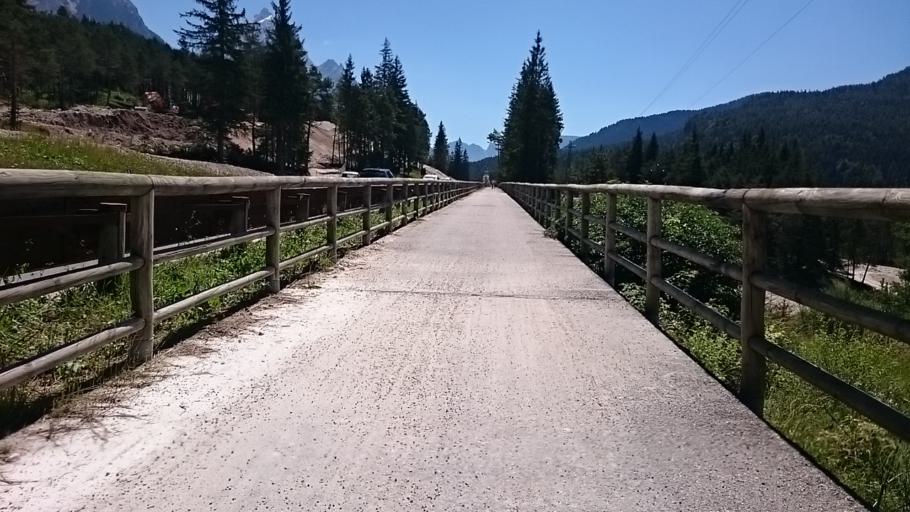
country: IT
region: Veneto
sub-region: Provincia di Belluno
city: Cortina d'Ampezzo
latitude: 46.5028
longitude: 12.1638
